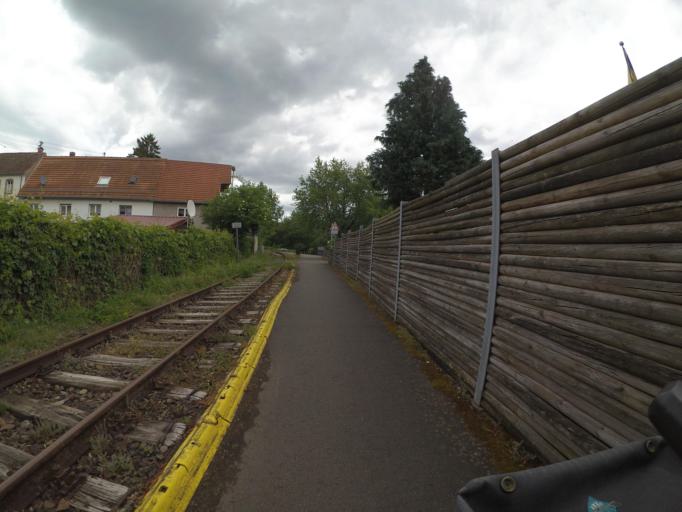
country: DE
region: Rheinland-Pfalz
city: Sankt Julian
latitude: 49.6122
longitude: 7.5292
